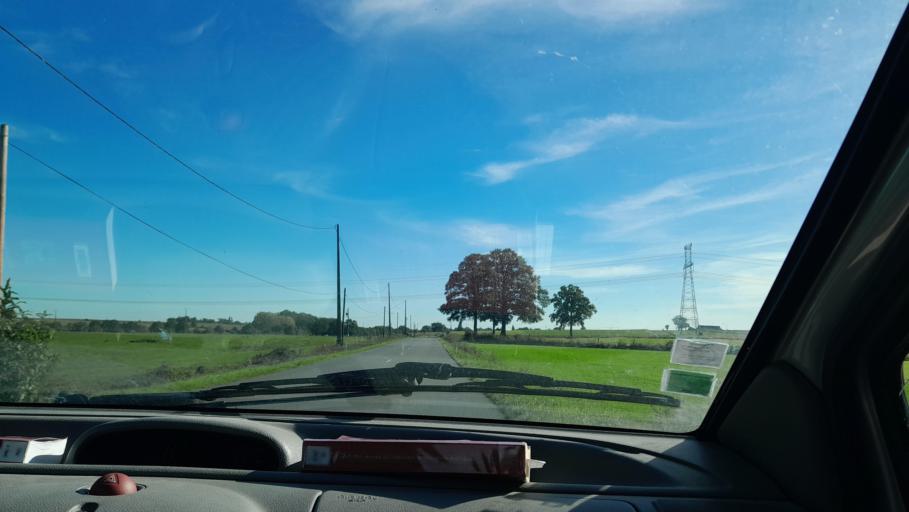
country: FR
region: Brittany
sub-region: Departement d'Ille-et-Vilaine
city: Argentre-du-Plessis
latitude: 48.0046
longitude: -1.1304
